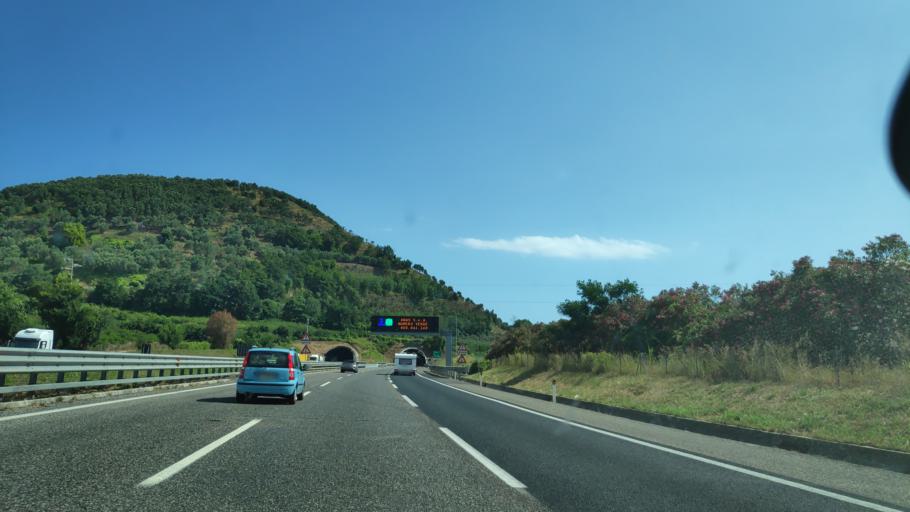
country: IT
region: Campania
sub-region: Provincia di Salerno
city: Pezzano-Filetta
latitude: 40.6802
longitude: 14.8570
